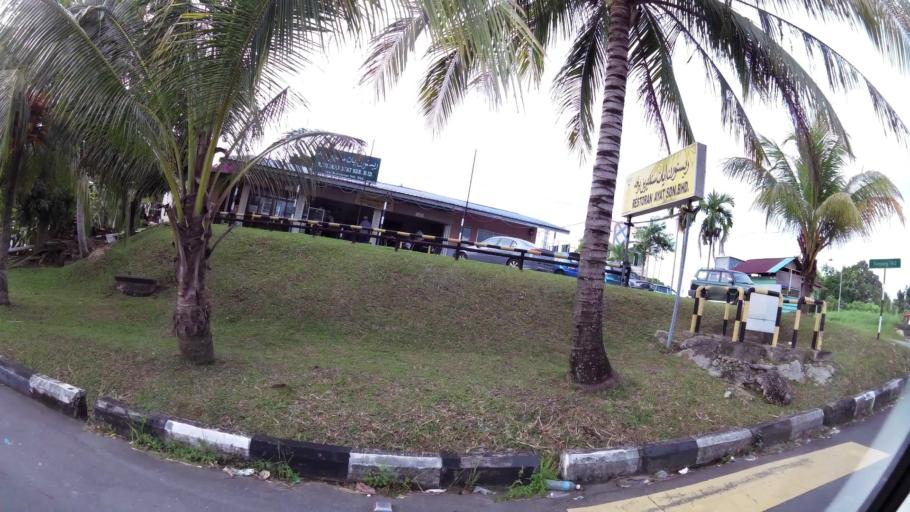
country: BN
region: Brunei and Muara
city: Bandar Seri Begawan
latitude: 4.8999
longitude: 114.8960
